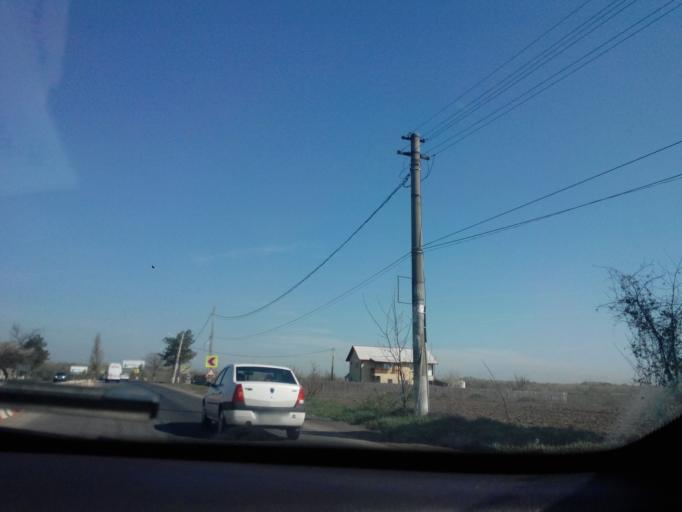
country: RO
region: Prahova
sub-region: Comuna Gorgota
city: Potigrafu
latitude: 44.7884
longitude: 26.0977
